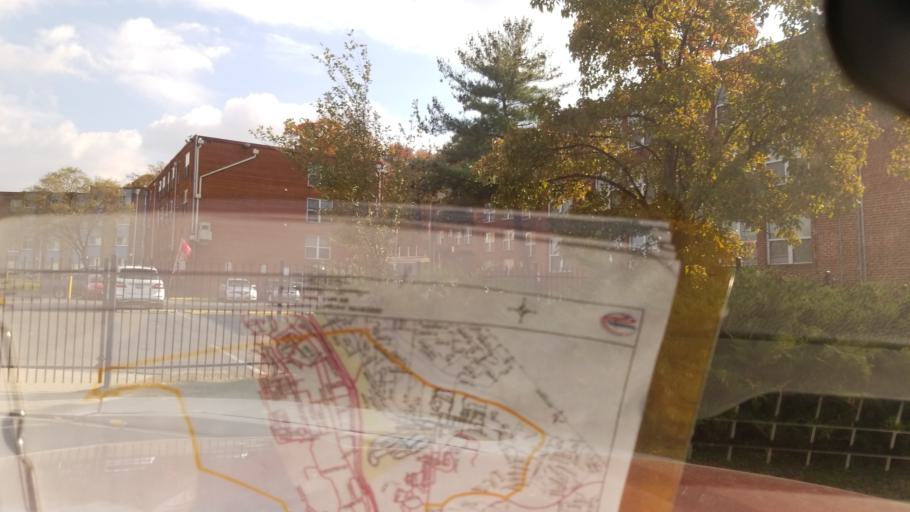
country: US
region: Maryland
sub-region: Prince George's County
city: Glassmanor
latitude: 38.8285
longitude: -76.9939
